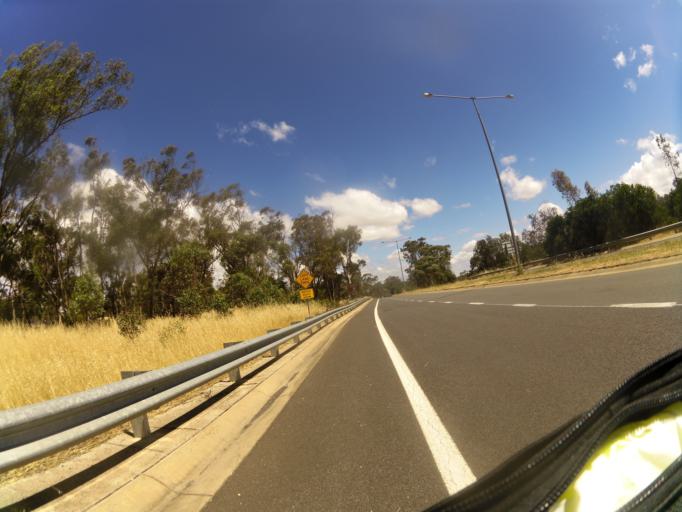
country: AU
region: Victoria
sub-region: Mount Alexander
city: Castlemaine
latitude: -37.0064
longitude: 144.2477
